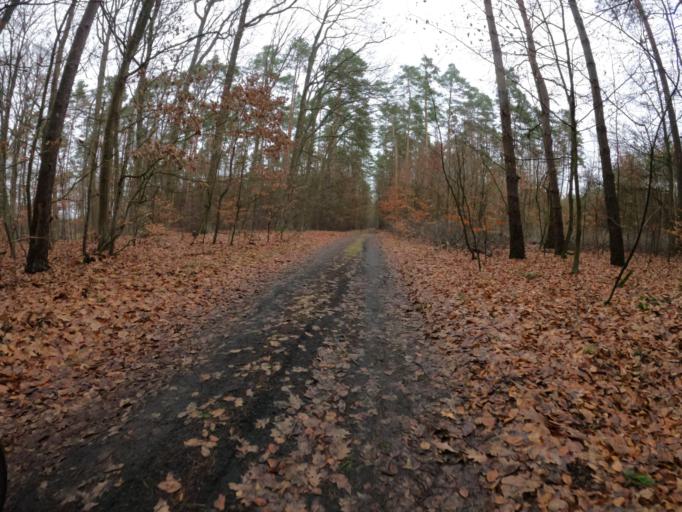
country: PL
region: West Pomeranian Voivodeship
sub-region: Powiat mysliborski
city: Debno
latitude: 52.7380
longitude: 14.7638
